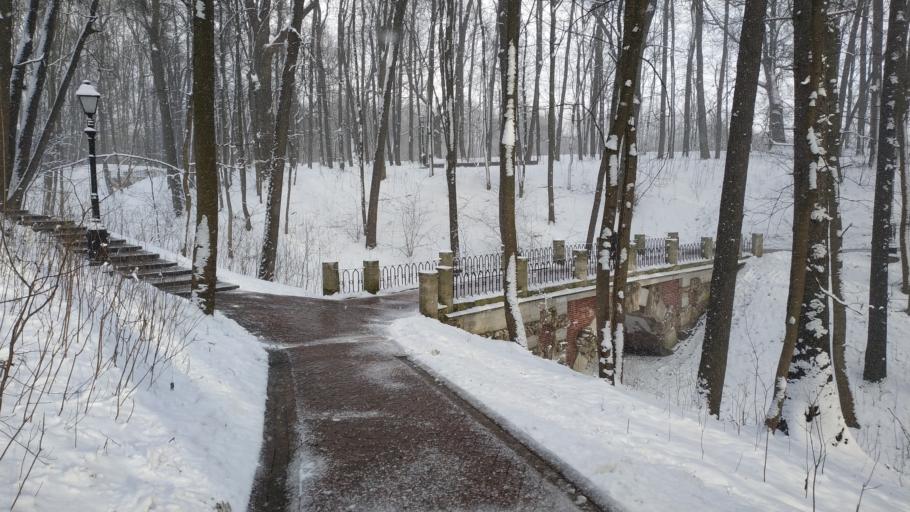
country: RU
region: Moscow
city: Orekhovo-Borisovo Severnoye
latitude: 55.6106
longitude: 37.6880
